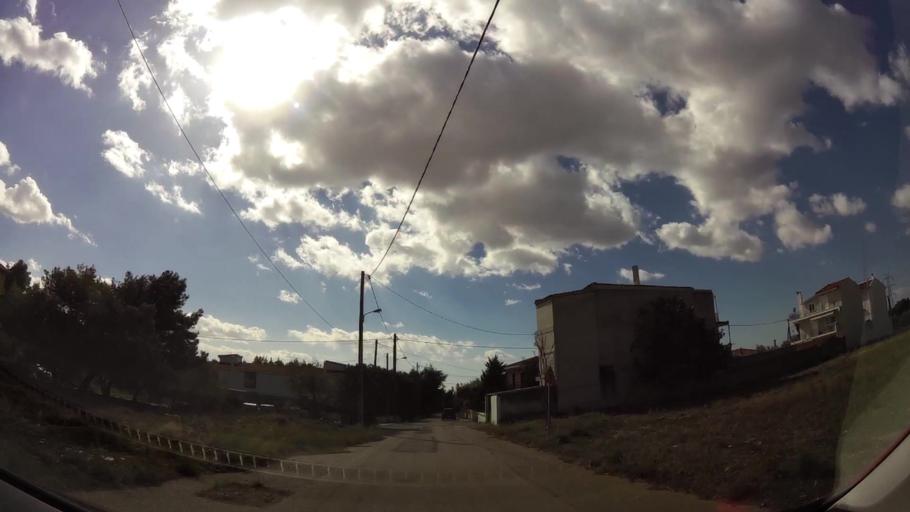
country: GR
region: Attica
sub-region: Nomarchia Anatolikis Attikis
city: Thrakomakedones
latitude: 38.1124
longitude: 23.7594
